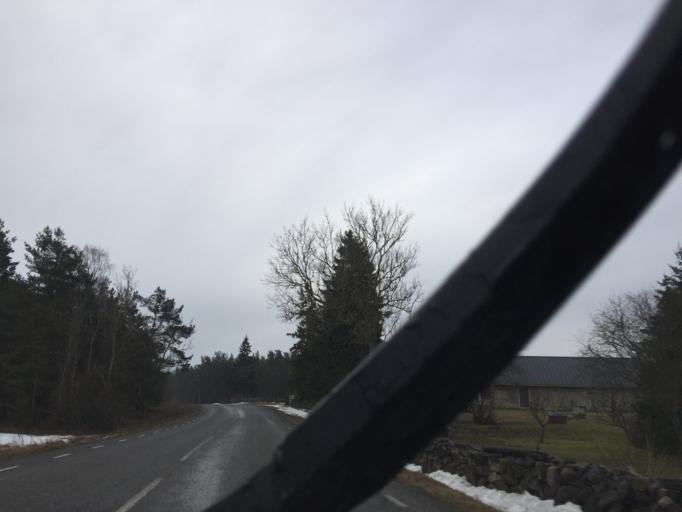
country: EE
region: Saare
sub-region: Orissaare vald
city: Orissaare
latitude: 58.6017
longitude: 22.9759
